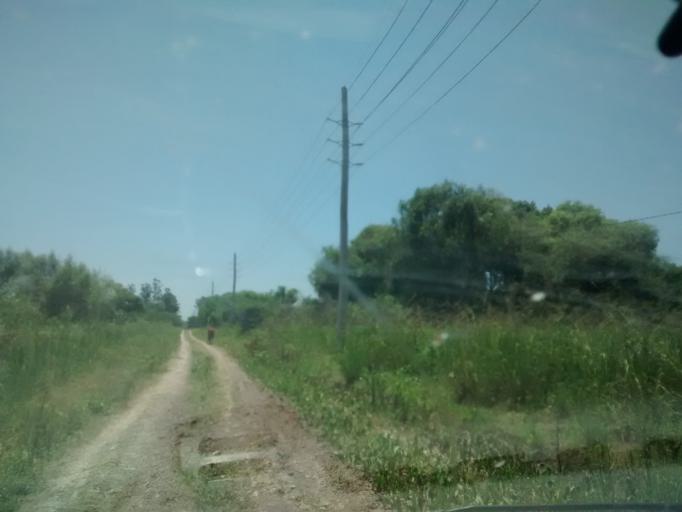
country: AR
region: Chaco
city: Fontana
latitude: -27.4222
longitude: -58.9884
